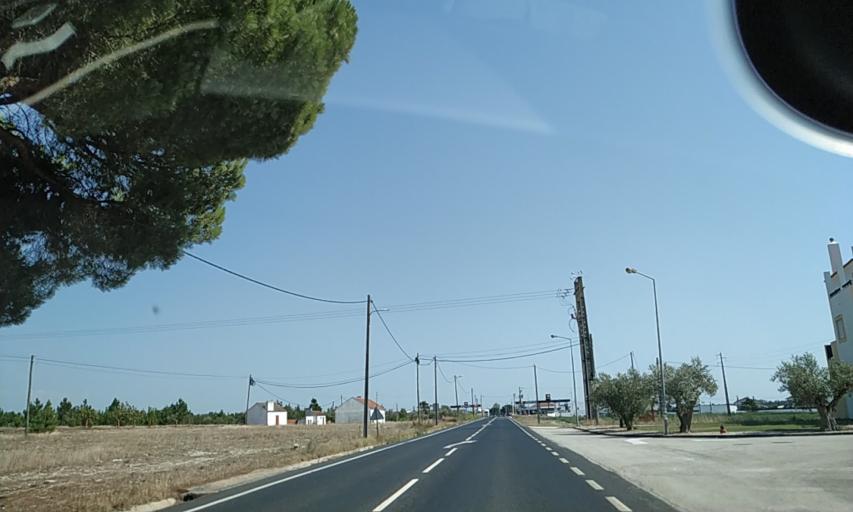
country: PT
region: Santarem
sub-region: Benavente
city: Poceirao
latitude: 38.7459
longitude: -8.6632
